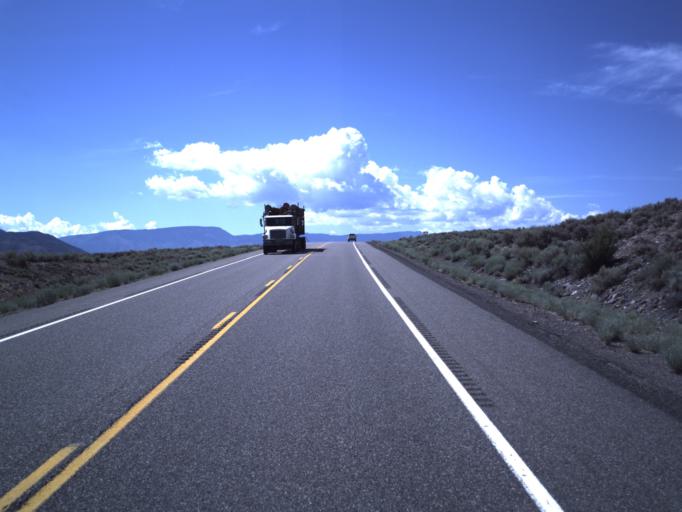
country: US
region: Utah
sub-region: Piute County
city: Junction
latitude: 38.3434
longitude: -112.2183
